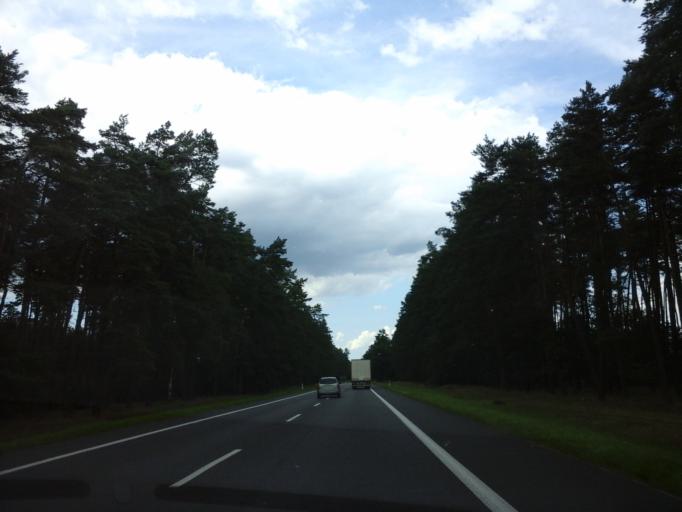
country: PL
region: West Pomeranian Voivodeship
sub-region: Powiat goleniowski
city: Goleniow
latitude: 53.6470
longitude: 14.8167
